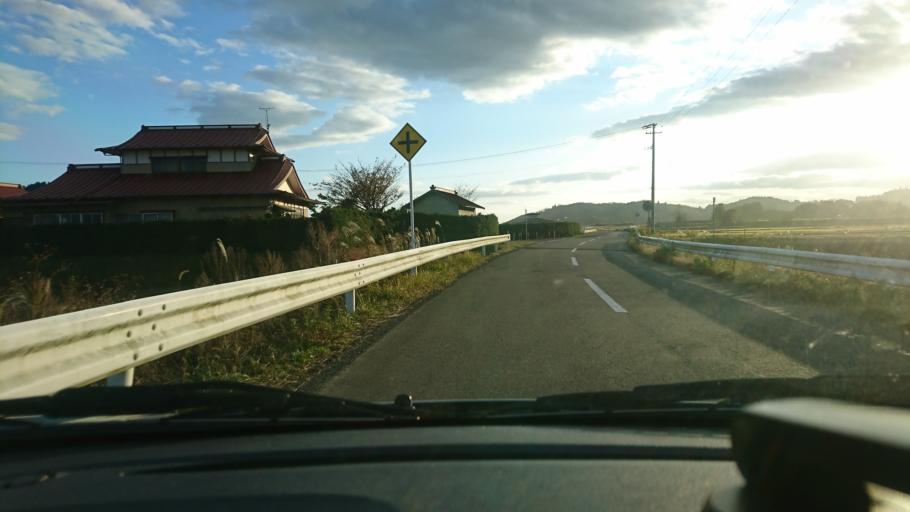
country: JP
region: Iwate
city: Ichinoseki
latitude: 38.7711
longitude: 141.2118
